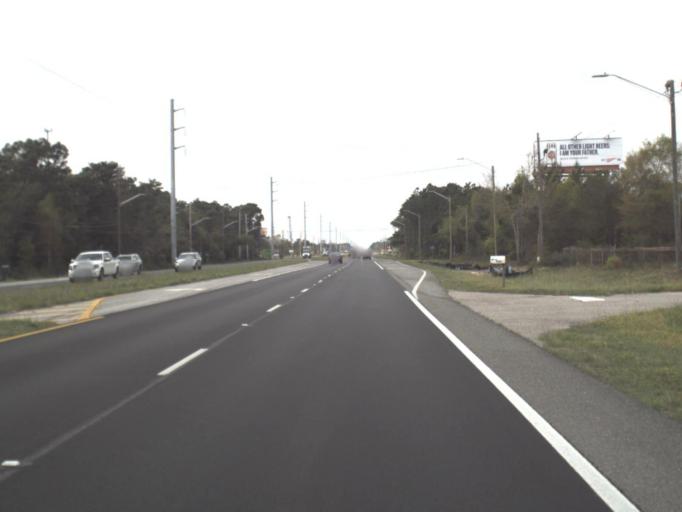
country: US
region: Florida
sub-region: Santa Rosa County
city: Tiger Point
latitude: 30.3948
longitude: -87.0338
